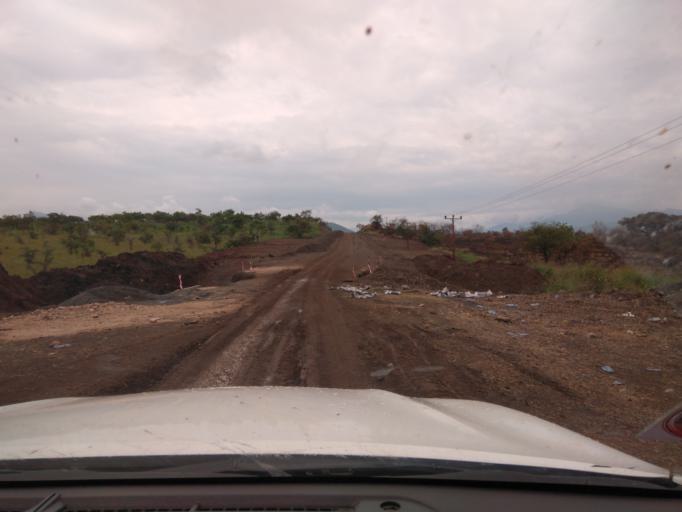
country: ET
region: Southern Nations, Nationalities, and People's Region
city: Felege Neway
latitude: 6.4264
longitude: 37.2535
